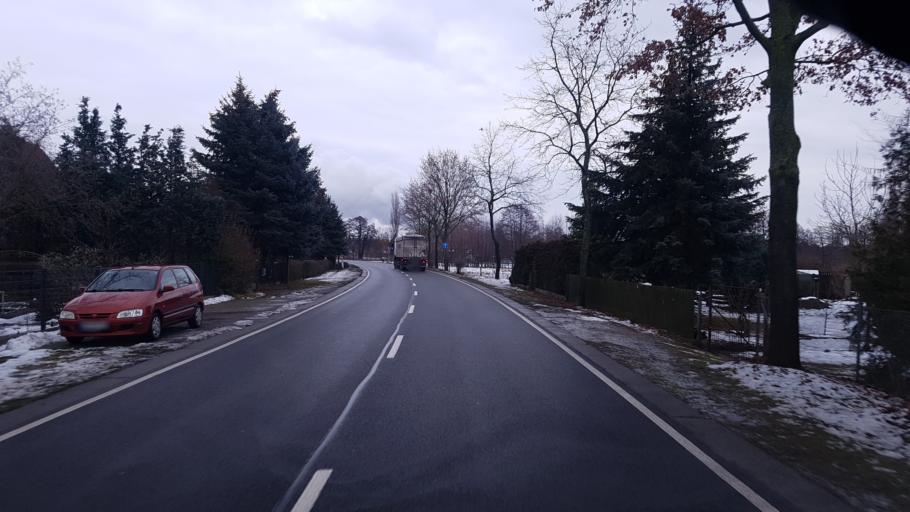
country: DE
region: Brandenburg
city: Peitz
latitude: 51.8500
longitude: 14.4151
